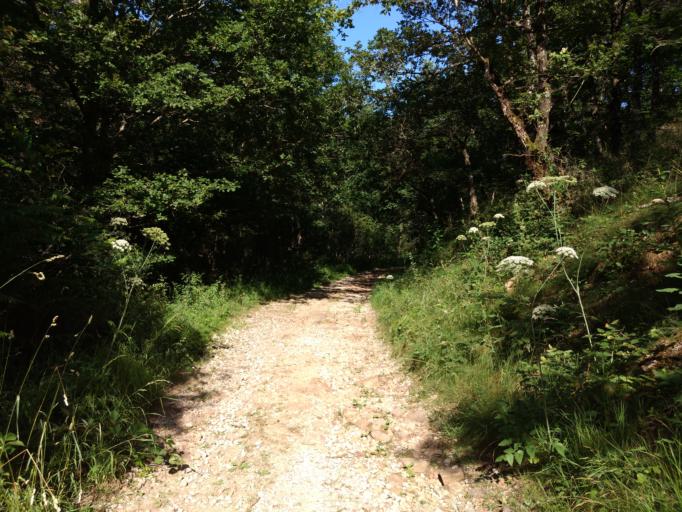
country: FR
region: Midi-Pyrenees
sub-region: Departement de l'Aveyron
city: La Loubiere
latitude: 44.3590
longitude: 2.6970
